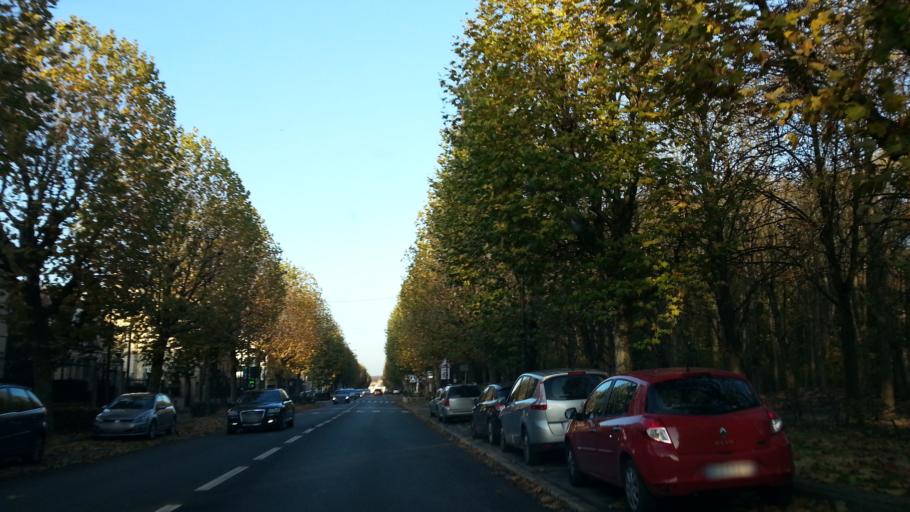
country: FR
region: Picardie
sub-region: Departement de l'Oise
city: Chantilly
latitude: 49.1889
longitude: 2.4624
